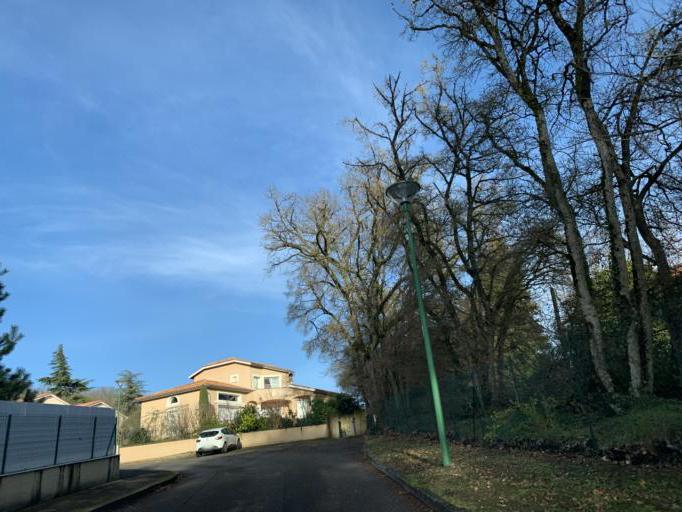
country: FR
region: Rhone-Alpes
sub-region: Departement de l'Ain
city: La Boisse
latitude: 45.8476
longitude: 5.0403
